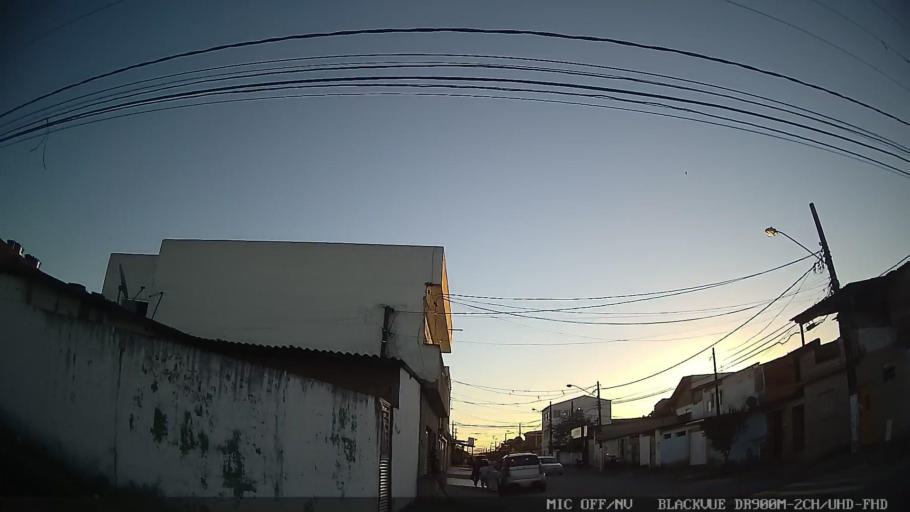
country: BR
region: Sao Paulo
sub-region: Guaruja
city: Guaruja
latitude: -23.9527
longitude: -46.2818
